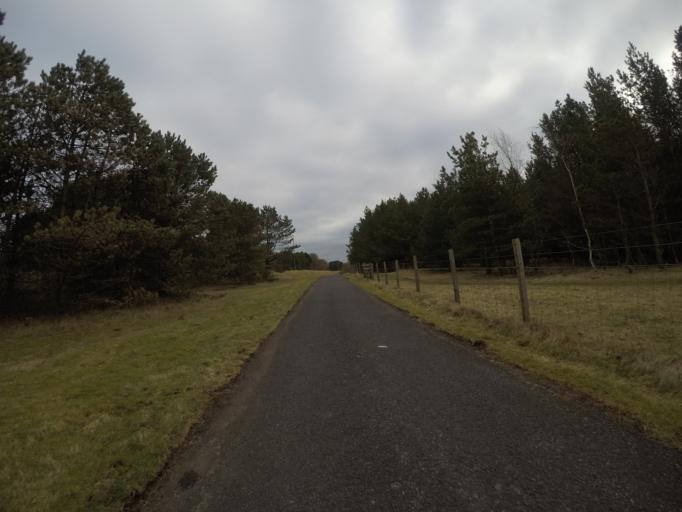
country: GB
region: Scotland
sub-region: North Ayrshire
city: Irvine
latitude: 55.5891
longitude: -4.6616
